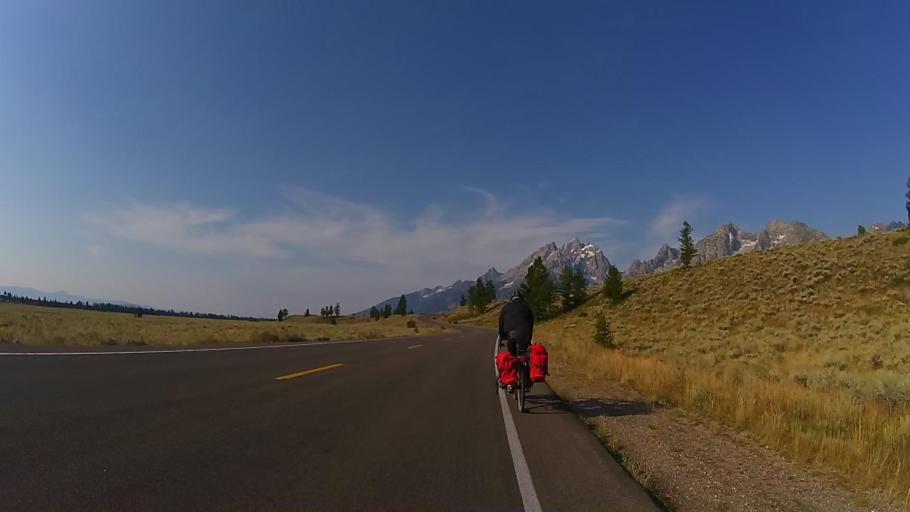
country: US
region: Wyoming
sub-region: Teton County
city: Moose Wilson Road
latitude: 43.7973
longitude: -110.6873
